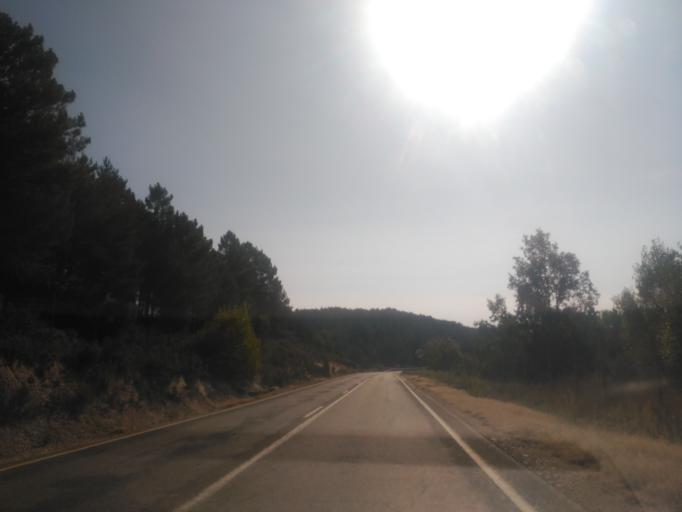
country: ES
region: Castille and Leon
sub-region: Provincia de Soria
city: Casarejos
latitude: 41.8029
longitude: -3.0443
